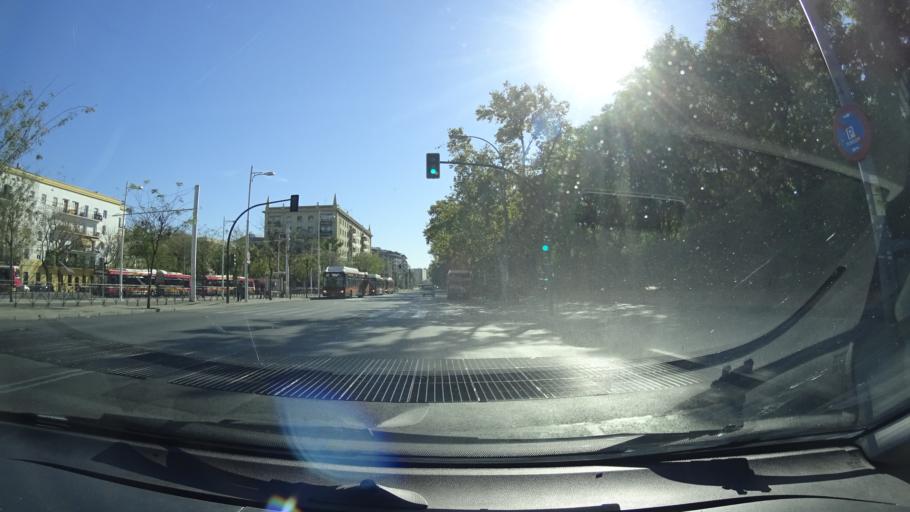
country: ES
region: Andalusia
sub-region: Provincia de Sevilla
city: Sevilla
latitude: 37.3803
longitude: -5.9860
